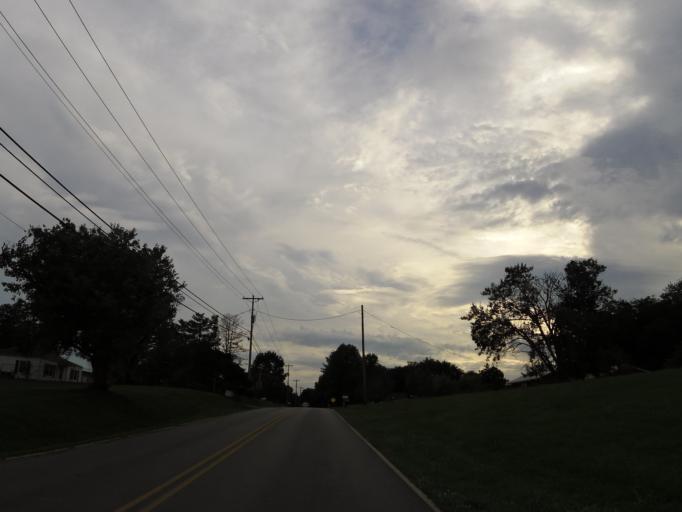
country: US
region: Tennessee
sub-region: Blount County
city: Maryville
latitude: 35.7229
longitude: -84.0438
